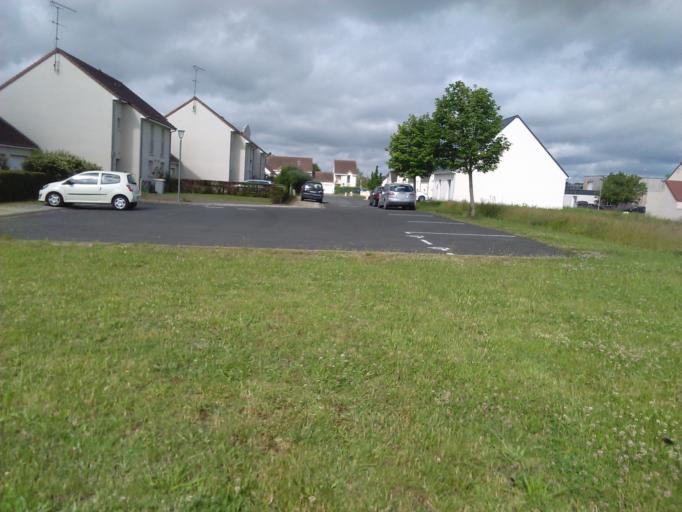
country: FR
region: Centre
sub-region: Departement du Loir-et-Cher
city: Naveil
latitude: 47.7927
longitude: 1.0357
